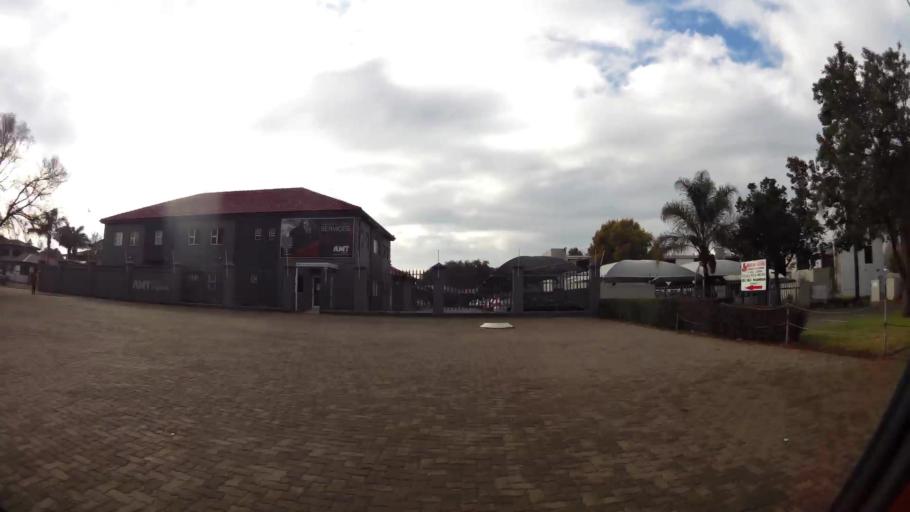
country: ZA
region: Gauteng
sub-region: Sedibeng District Municipality
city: Vanderbijlpark
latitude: -26.7011
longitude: 27.8313
